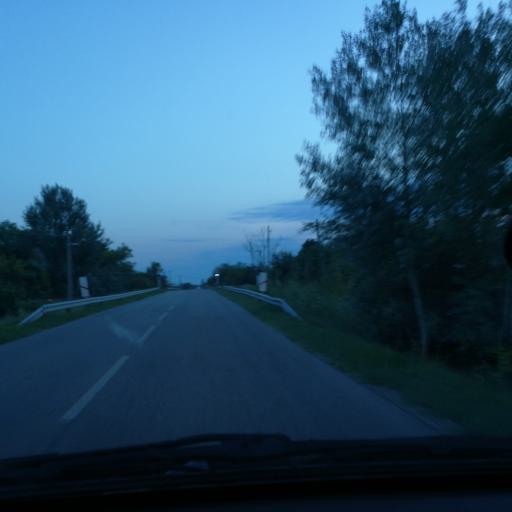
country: HU
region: Bacs-Kiskun
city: Csaszartoltes
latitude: 46.5241
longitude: 19.1199
